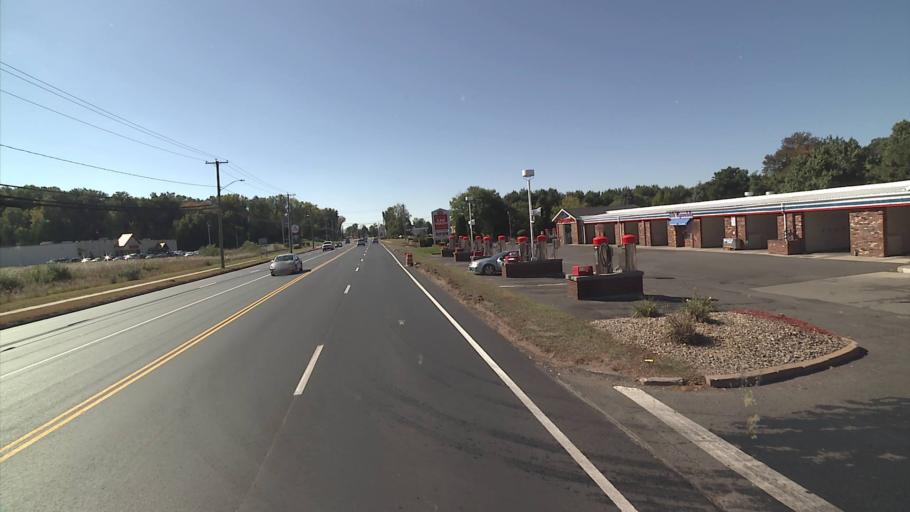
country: US
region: Connecticut
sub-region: Tolland County
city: Rockville
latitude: 41.8433
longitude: -72.4880
